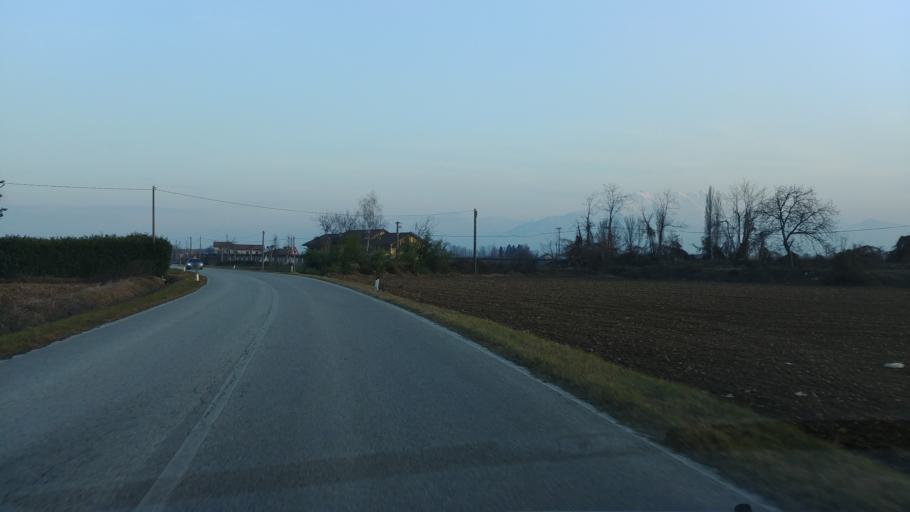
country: IT
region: Piedmont
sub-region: Provincia di Cuneo
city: San Defendente
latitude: 44.4080
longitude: 7.5175
